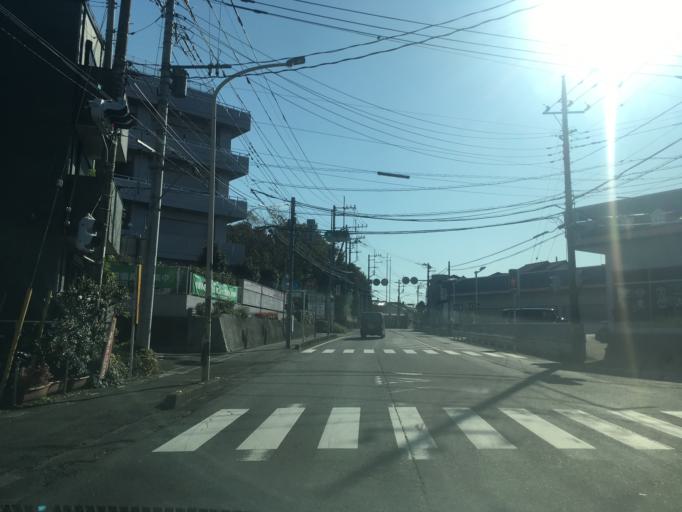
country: JP
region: Saitama
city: Kawagoe
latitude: 35.8936
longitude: 139.4793
